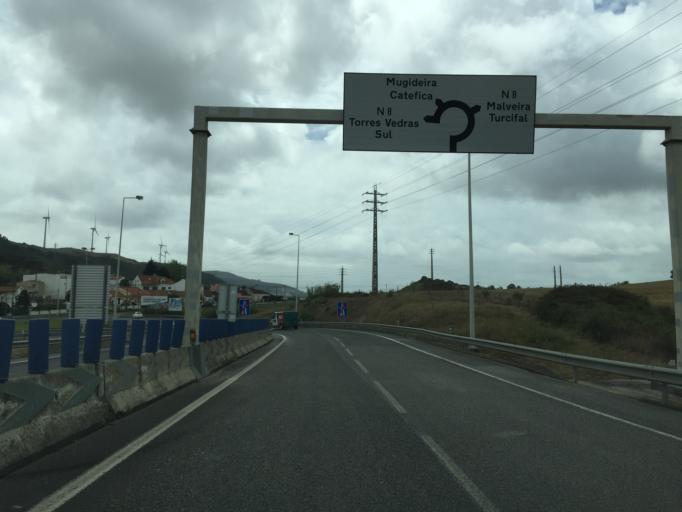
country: PT
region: Lisbon
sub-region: Torres Vedras
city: Torres Vedras
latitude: 39.0607
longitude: -9.2424
